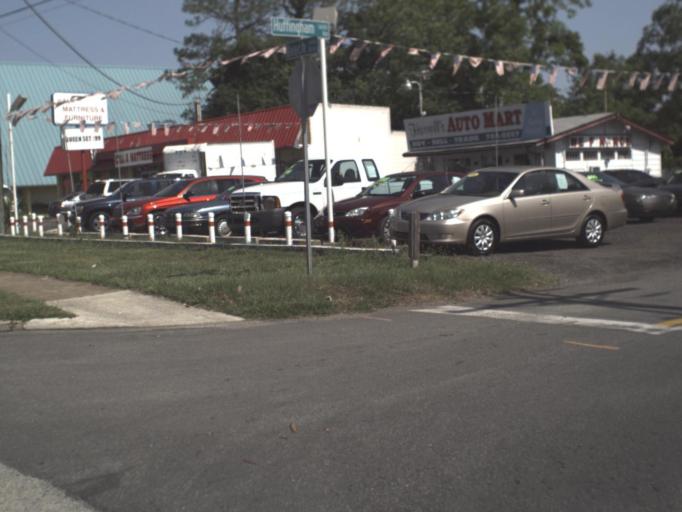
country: US
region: Florida
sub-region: Duval County
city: Jacksonville
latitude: 30.2922
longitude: -81.6007
